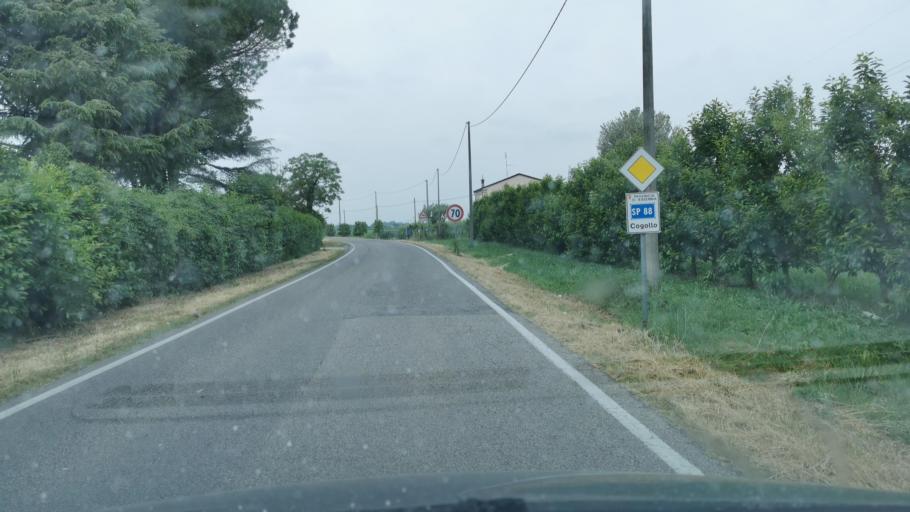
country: IT
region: Emilia-Romagna
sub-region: Provincia di Ravenna
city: Santerno
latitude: 44.4338
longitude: 12.0391
